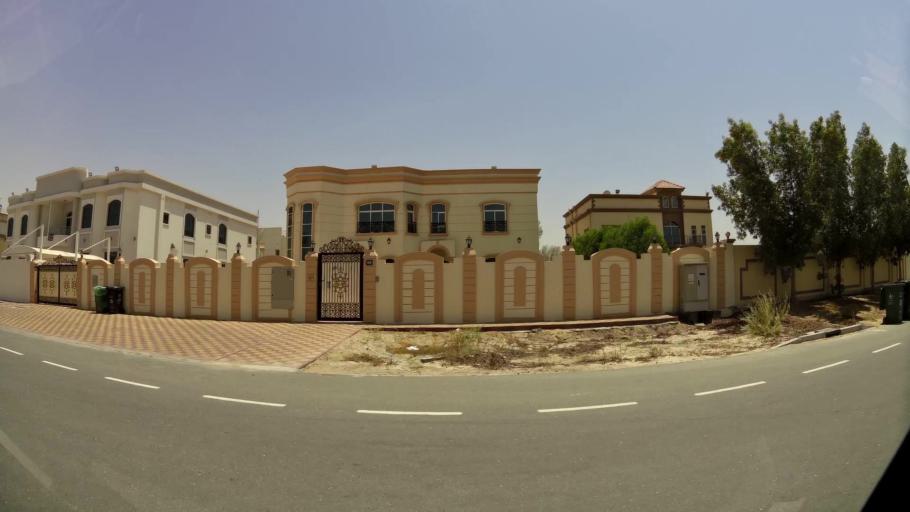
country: AE
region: Dubai
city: Dubai
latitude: 25.0875
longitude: 55.2115
